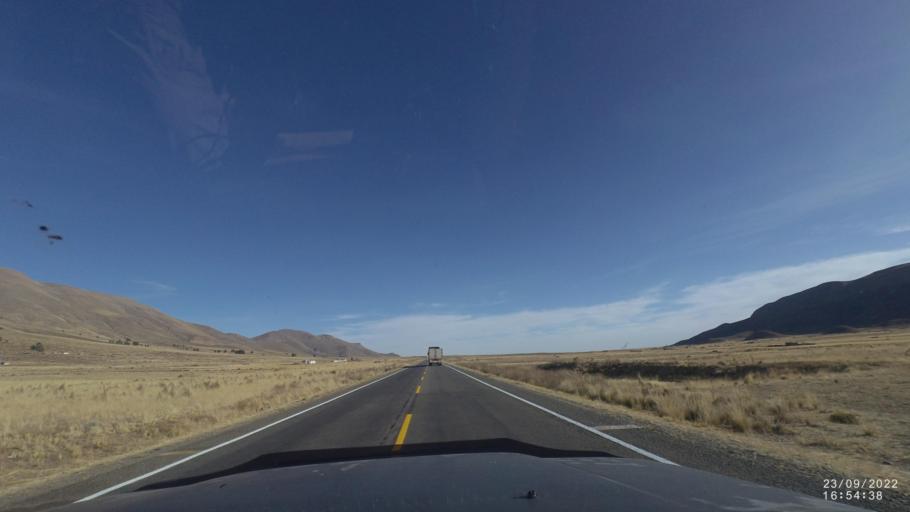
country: BO
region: Oruro
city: Poopo
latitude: -18.4670
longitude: -66.9686
